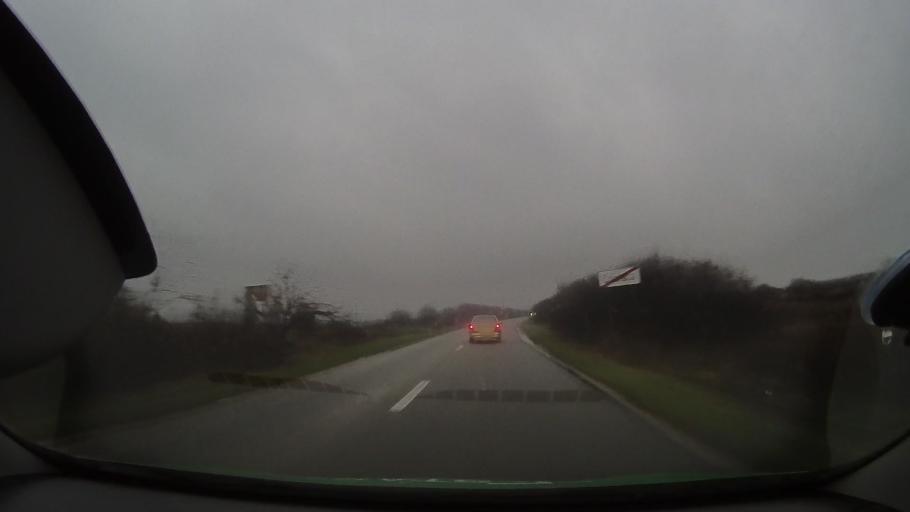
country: RO
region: Arad
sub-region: Comuna Craiova
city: Craiova
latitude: 46.5480
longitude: 21.9601
